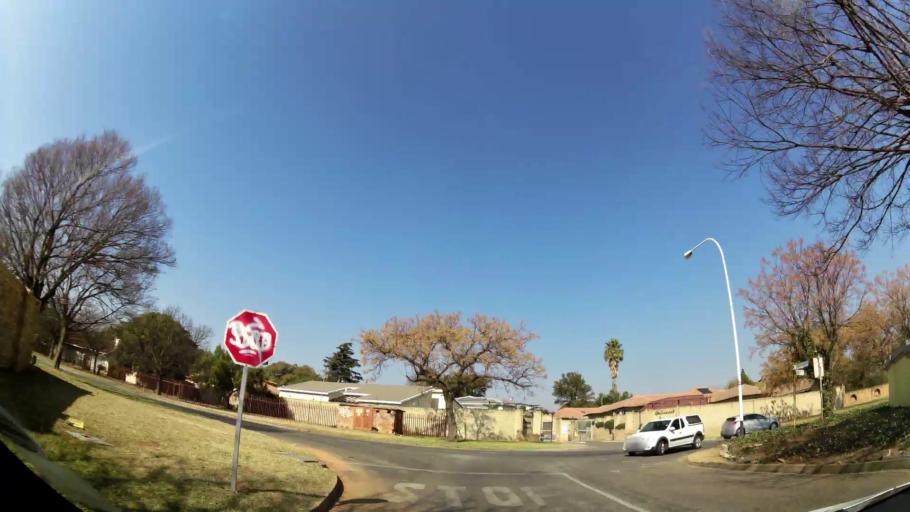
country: ZA
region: Gauteng
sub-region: Ekurhuleni Metropolitan Municipality
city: Boksburg
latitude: -26.2456
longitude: 28.2512
